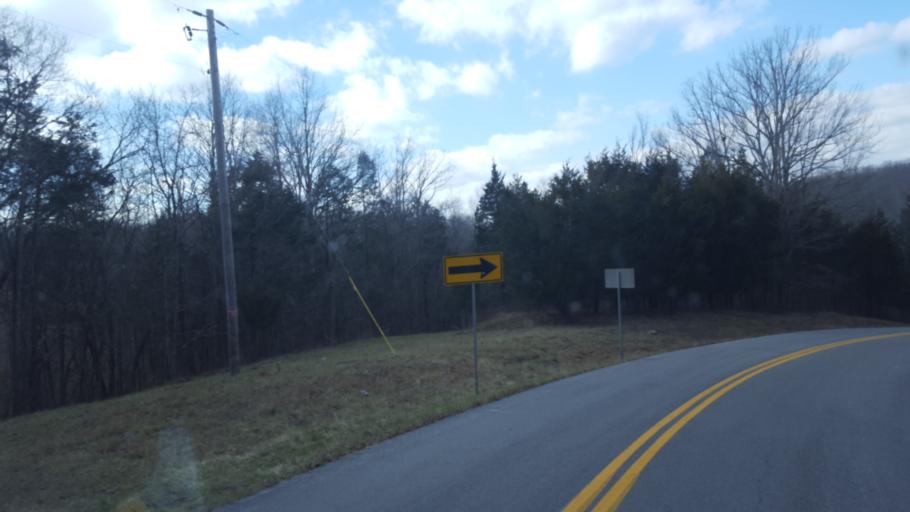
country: US
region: Kentucky
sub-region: Owen County
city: Owenton
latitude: 38.3898
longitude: -84.9591
